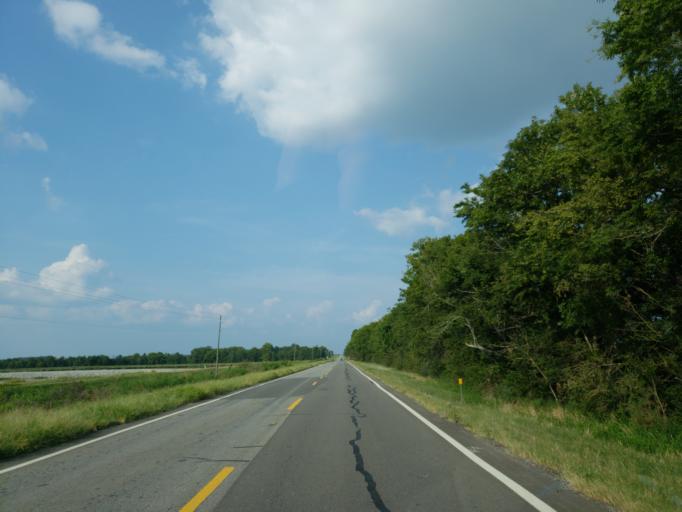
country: US
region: Alabama
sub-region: Greene County
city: Eutaw
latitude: 32.7962
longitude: -87.9667
